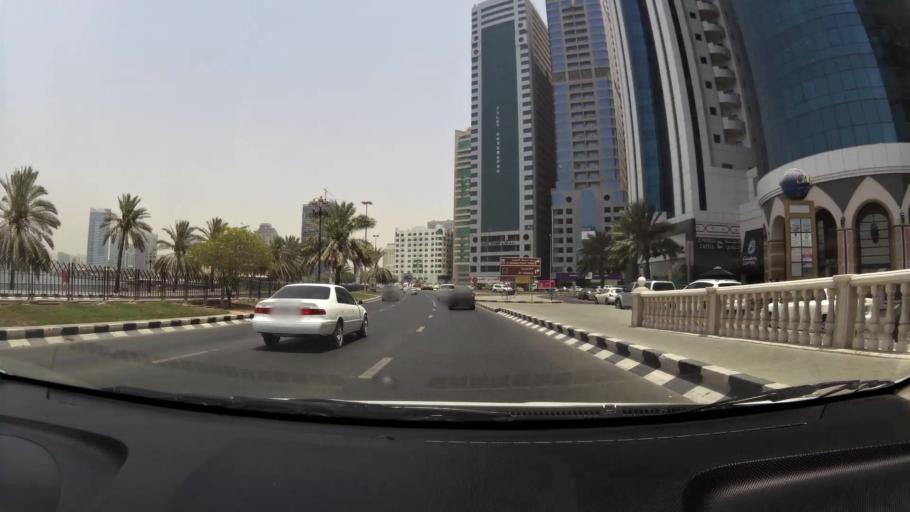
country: AE
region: Ash Shariqah
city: Sharjah
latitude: 25.3243
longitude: 55.3825
